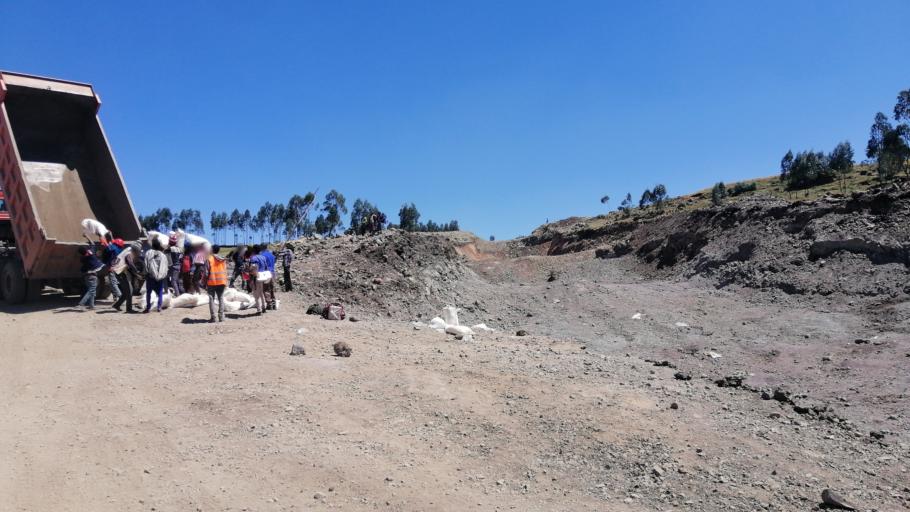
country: ET
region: Amhara
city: Debre Tabor
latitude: 11.4204
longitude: 38.2143
